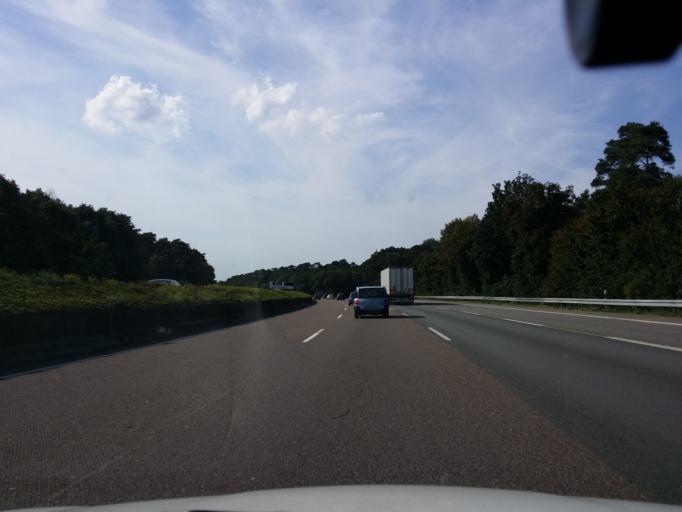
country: DE
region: North Rhine-Westphalia
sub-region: Regierungsbezirk Koln
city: Rath
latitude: 50.9136
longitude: 7.1083
